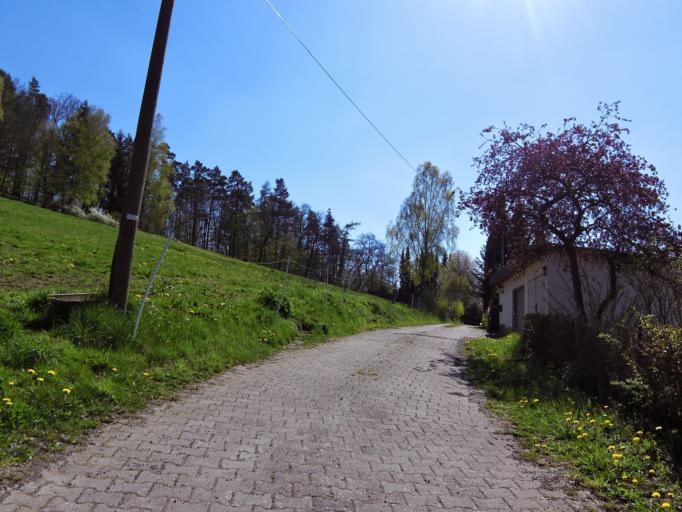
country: DE
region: Thuringia
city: Wolfsburg-Unkeroda
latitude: 50.9400
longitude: 10.2712
